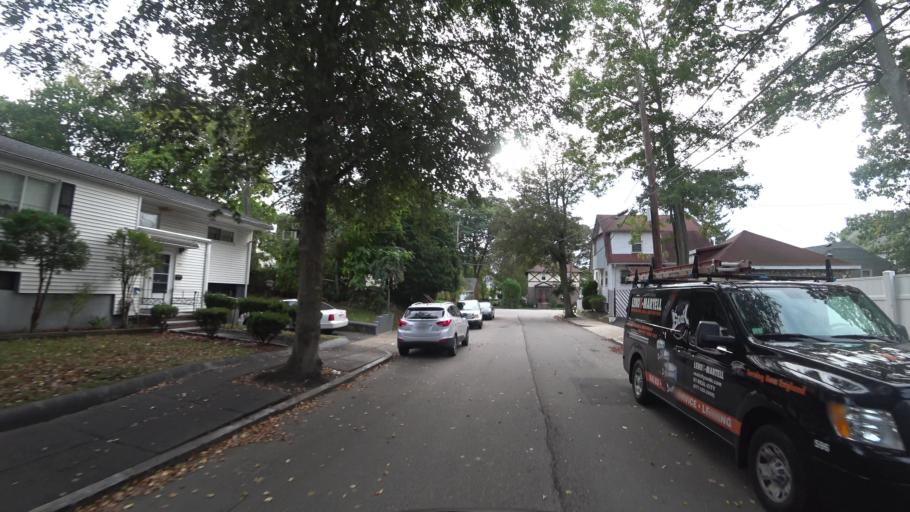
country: US
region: Massachusetts
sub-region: Norfolk County
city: Milton
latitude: 42.2722
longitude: -71.1010
